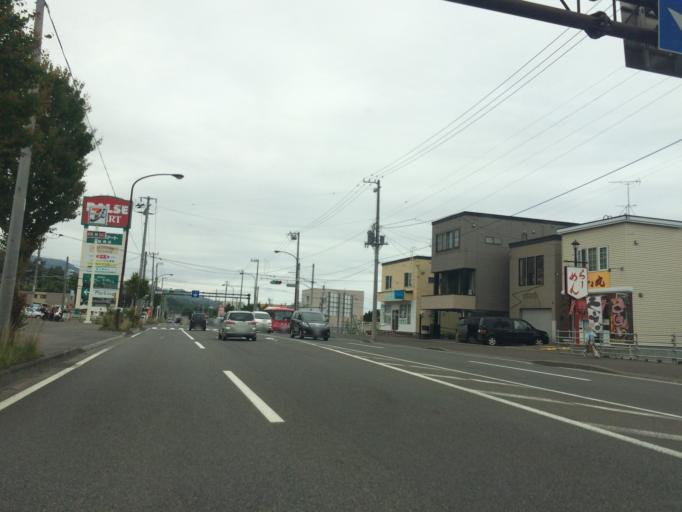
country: JP
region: Hokkaido
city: Otaru
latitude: 43.1429
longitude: 141.1478
